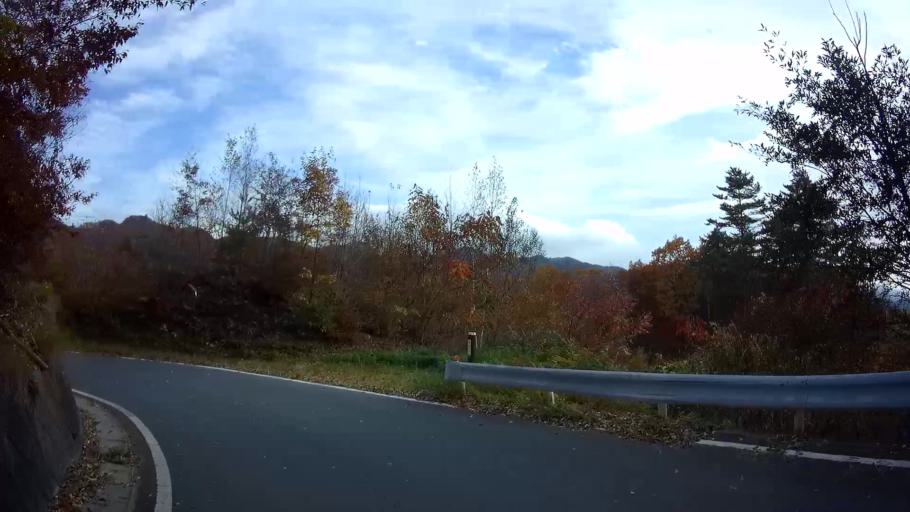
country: JP
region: Gunma
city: Nakanojomachi
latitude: 36.6319
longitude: 138.6473
